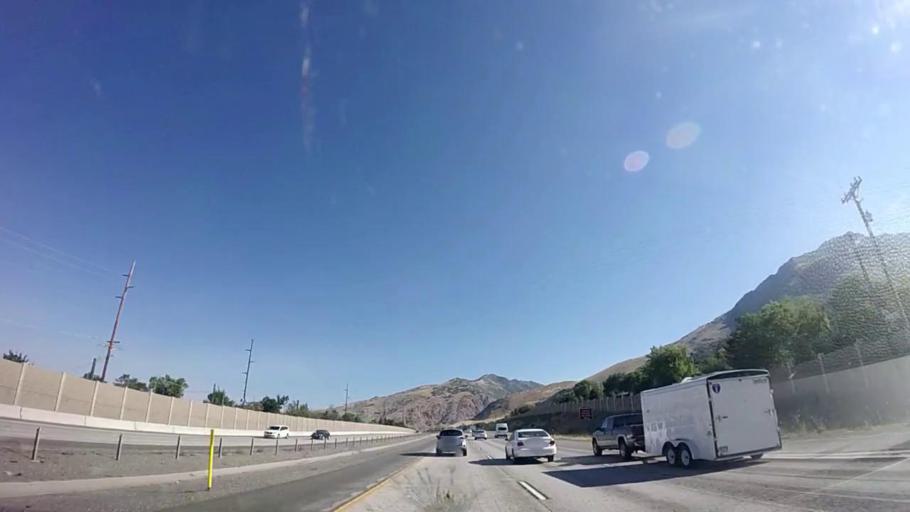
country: US
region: Utah
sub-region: Salt Lake County
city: Mount Olympus
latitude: 40.6935
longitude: -111.7964
